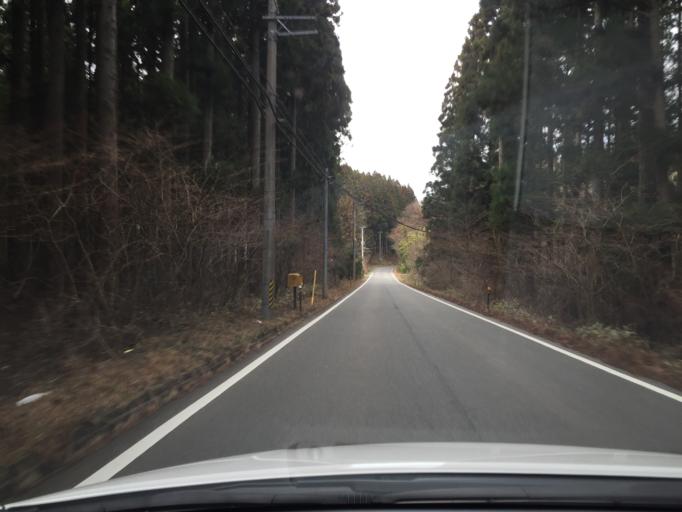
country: JP
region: Fukushima
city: Iwaki
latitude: 37.1126
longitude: 140.7798
